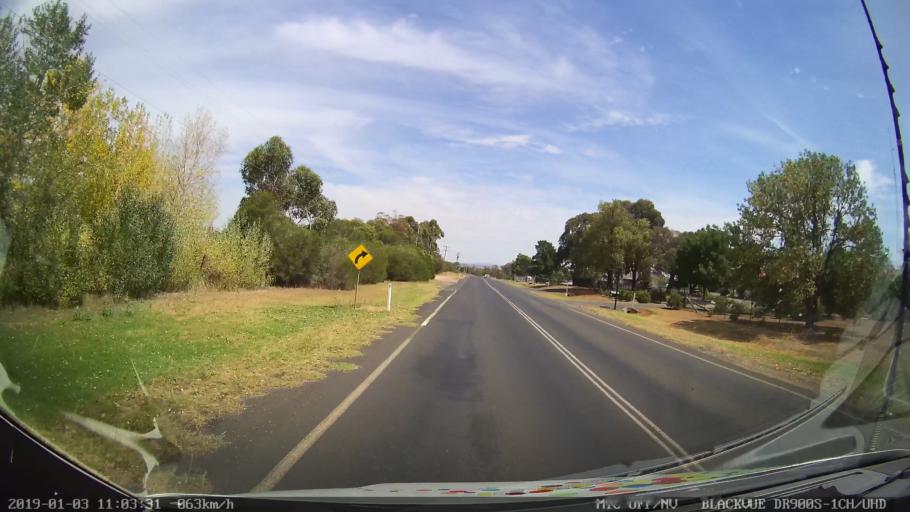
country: AU
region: New South Wales
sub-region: Young
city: Young
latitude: -34.2898
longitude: 148.2942
